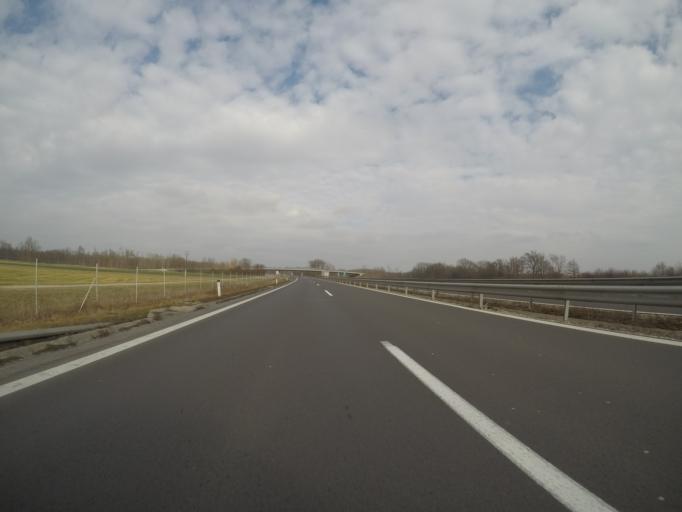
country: SI
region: Krizevci
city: Krizevci pri Ljutomeru
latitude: 46.5965
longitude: 16.1173
